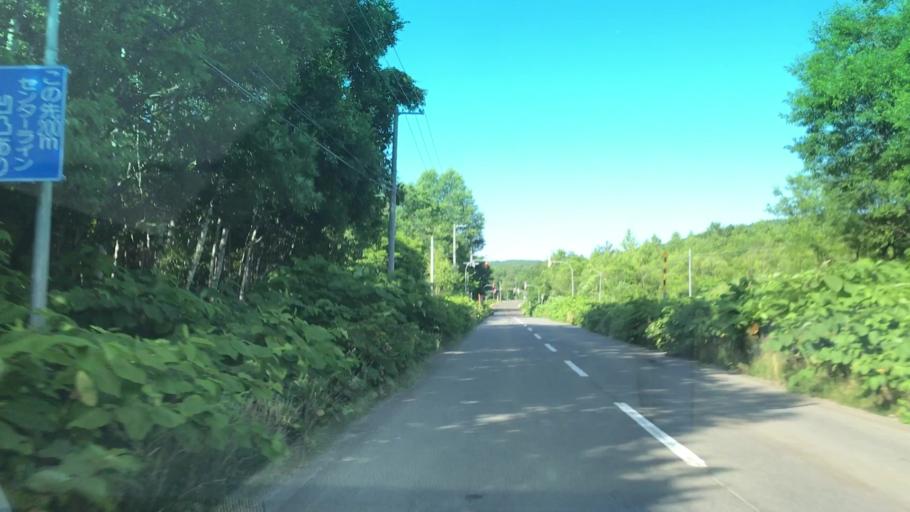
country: JP
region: Hokkaido
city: Yoichi
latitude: 43.0586
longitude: 140.8672
